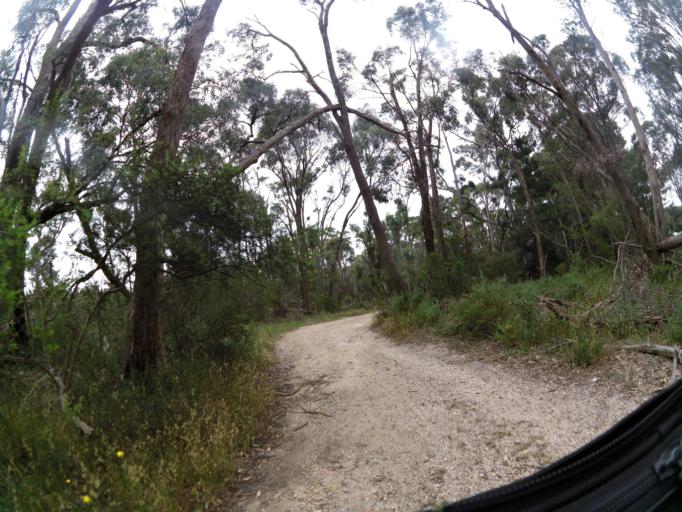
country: AU
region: Victoria
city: Brown Hill
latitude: -37.4377
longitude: 143.9064
